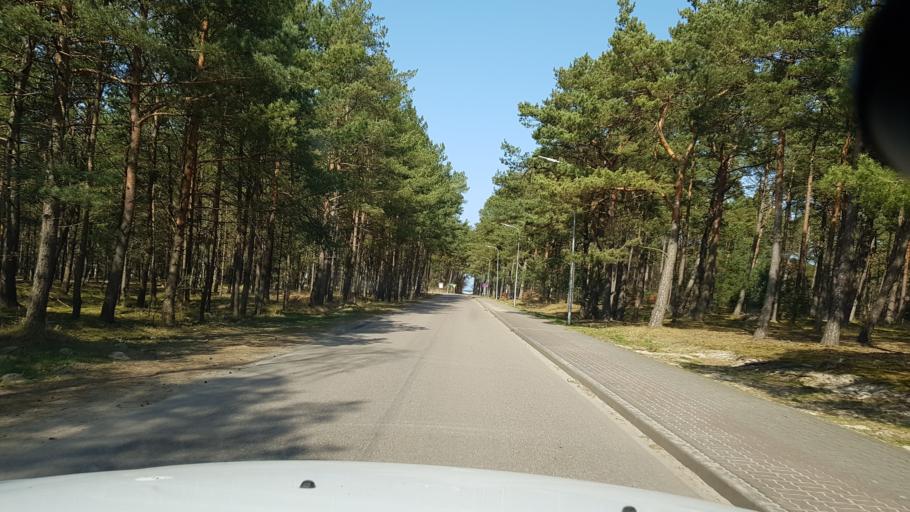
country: PL
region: West Pomeranian Voivodeship
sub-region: Powiat slawienski
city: Darlowo
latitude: 54.5245
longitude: 16.5104
